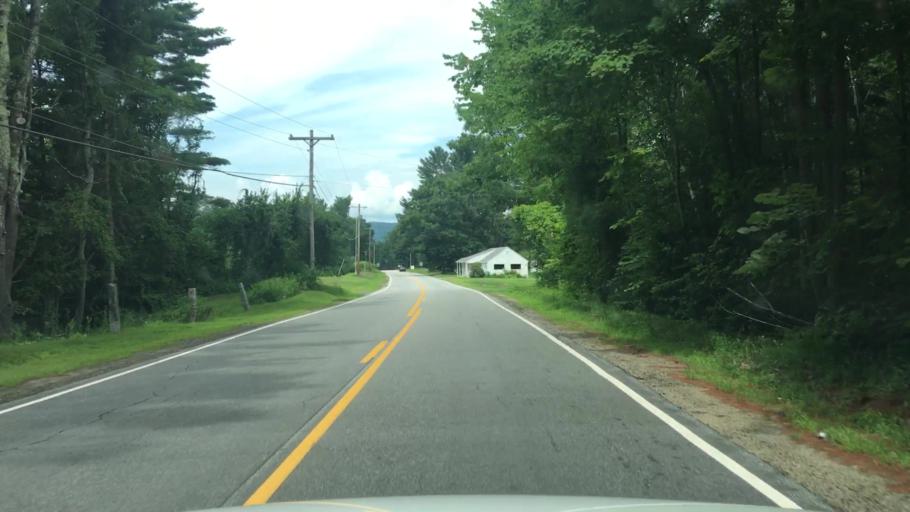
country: US
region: New Hampshire
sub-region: Grafton County
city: Rumney
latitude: 43.7826
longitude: -71.7642
